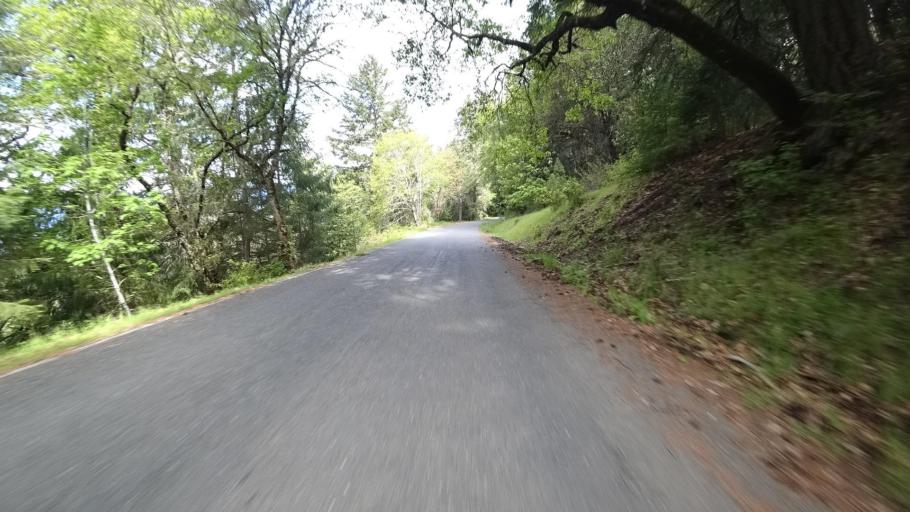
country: US
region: California
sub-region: Humboldt County
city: Redway
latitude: 40.1689
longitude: -123.5640
